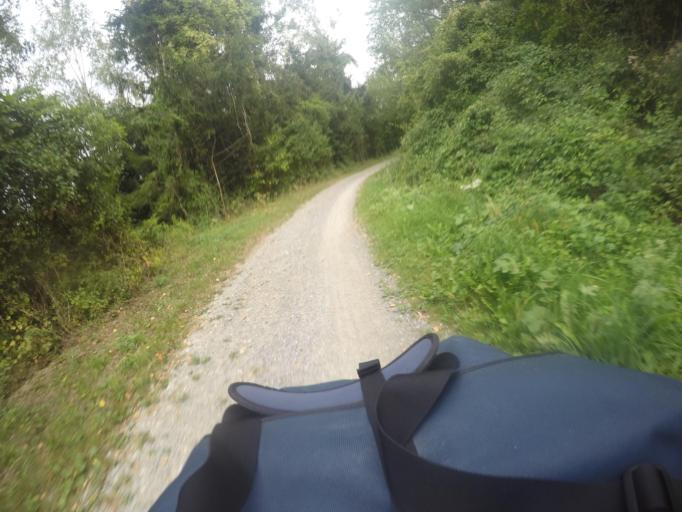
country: DE
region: North Rhine-Westphalia
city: Haan
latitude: 51.2140
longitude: 6.9985
